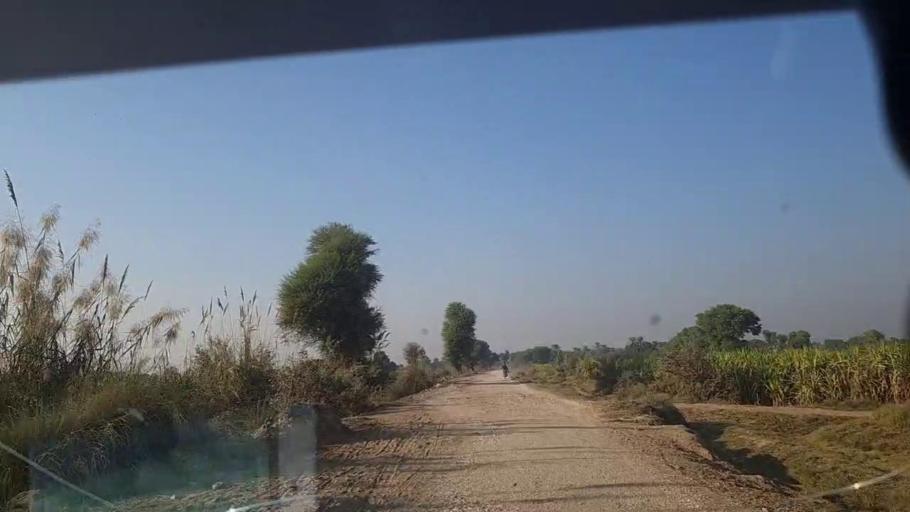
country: PK
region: Sindh
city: Sobhadero
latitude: 27.2636
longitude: 68.3500
